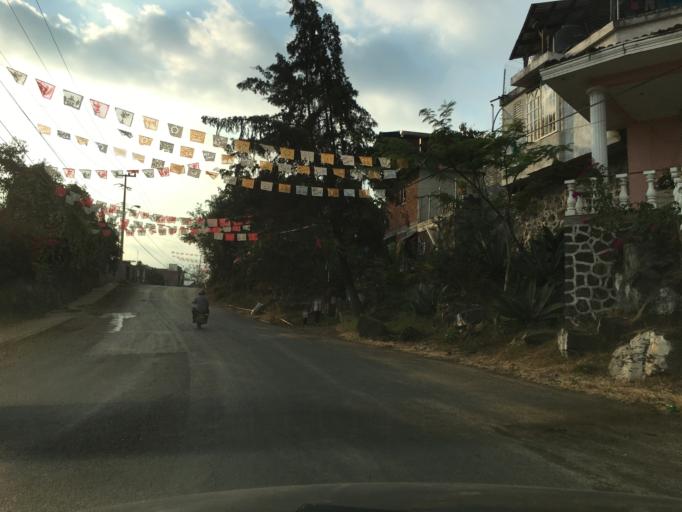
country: MX
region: Michoacan
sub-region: Ziracuaretiro
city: Patuan
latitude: 19.4444
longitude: -101.8856
